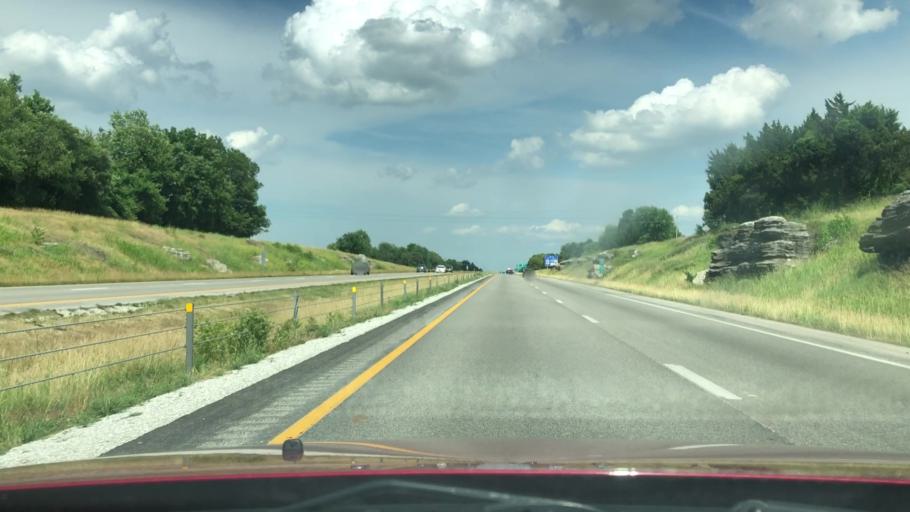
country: US
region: Missouri
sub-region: Greene County
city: Springfield
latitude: 37.2502
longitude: -93.2855
